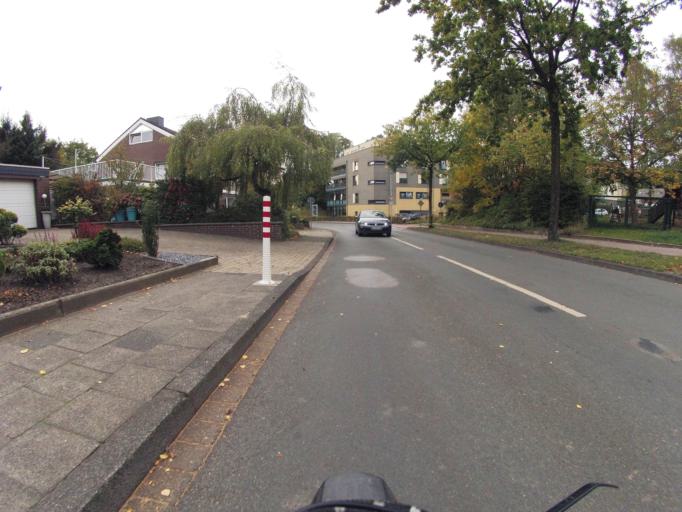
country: DE
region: North Rhine-Westphalia
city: Ibbenburen
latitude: 52.2895
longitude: 7.7261
